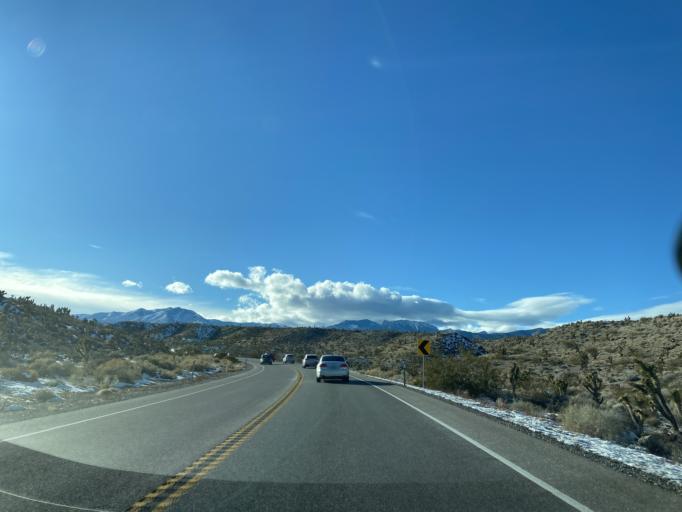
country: US
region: Nevada
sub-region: Clark County
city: Summerlin South
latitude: 36.2798
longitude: -115.4645
